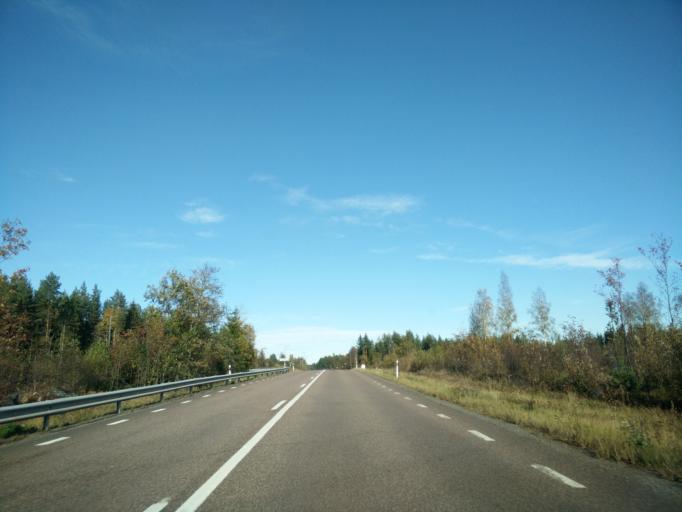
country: SE
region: Gaevleborg
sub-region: Hudiksvalls Kommun
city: Iggesund
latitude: 61.5983
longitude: 17.0420
